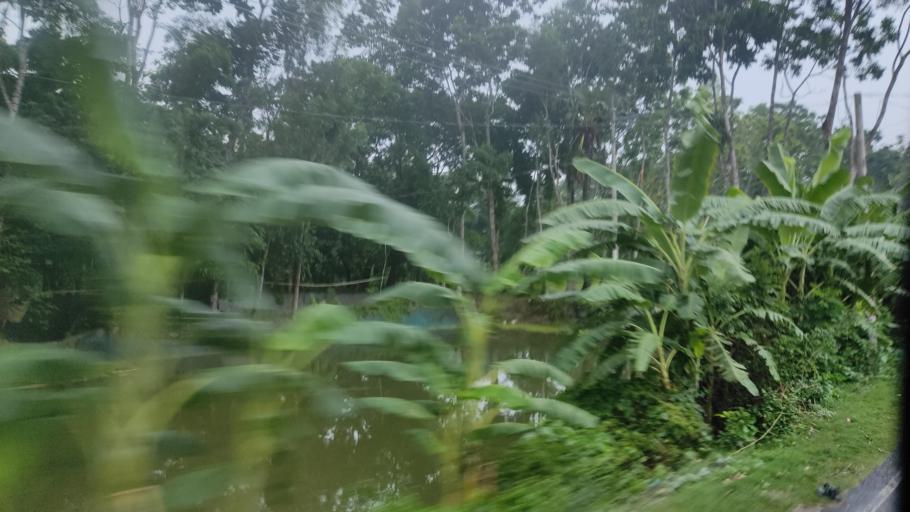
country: BD
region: Barisal
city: Bhandaria
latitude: 22.3039
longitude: 90.3245
